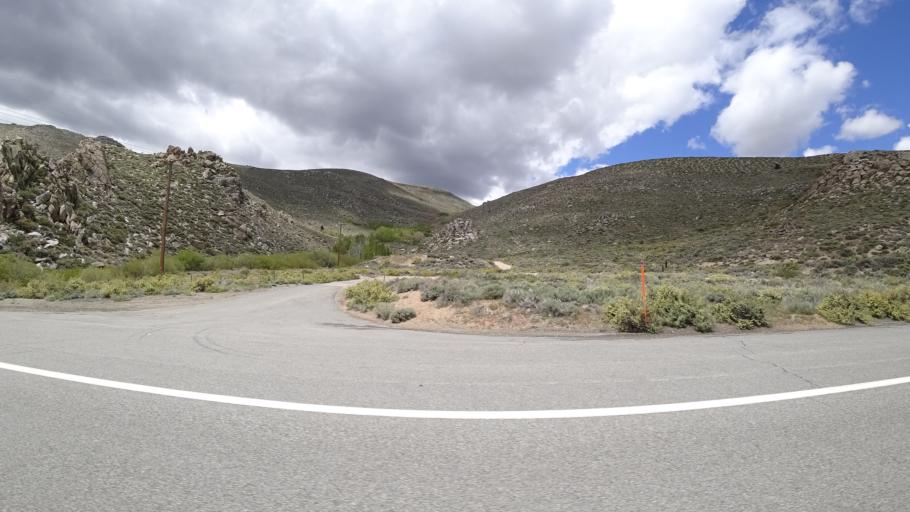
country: US
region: California
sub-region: Mono County
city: Bridgeport
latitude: 38.0704
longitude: -119.1697
